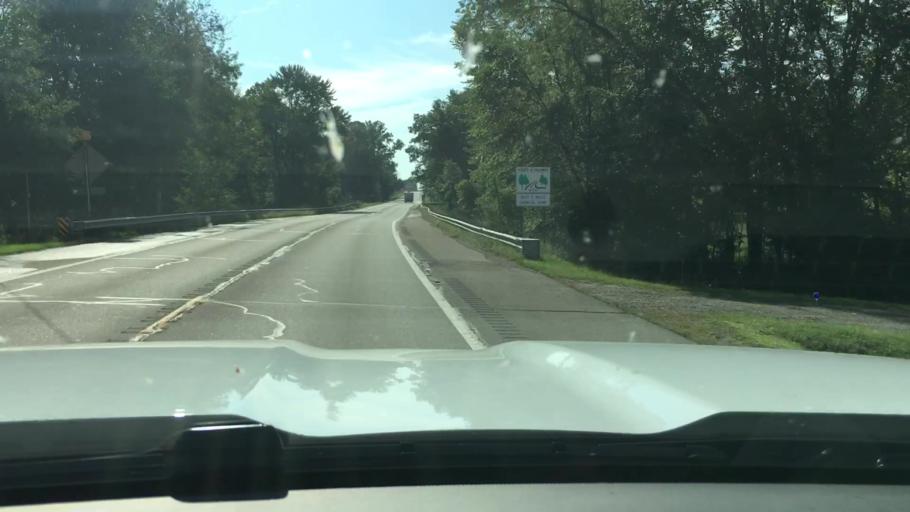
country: US
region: Michigan
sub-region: Montcalm County
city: Edmore
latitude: 43.4253
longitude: -85.1458
